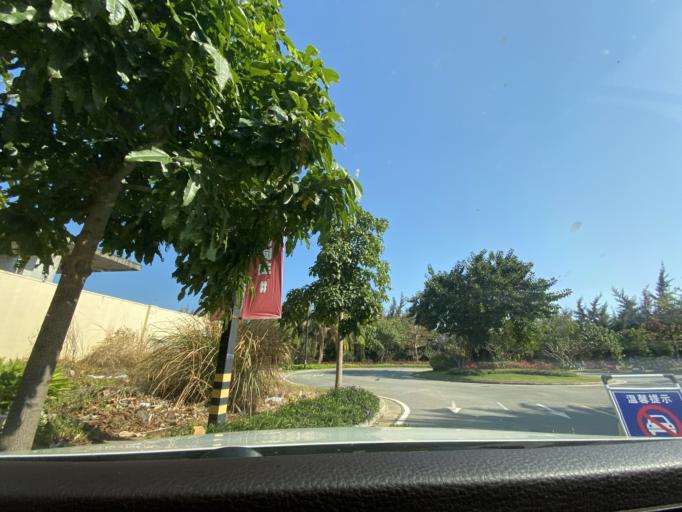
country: CN
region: Hainan
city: Yingzhou
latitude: 18.4077
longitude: 109.8815
